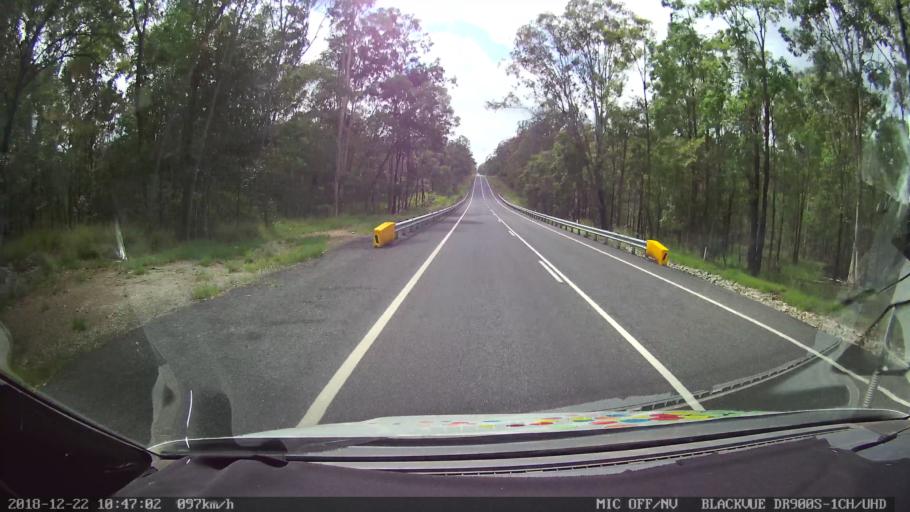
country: AU
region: New South Wales
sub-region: Clarence Valley
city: South Grafton
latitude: -29.6706
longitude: 152.8333
